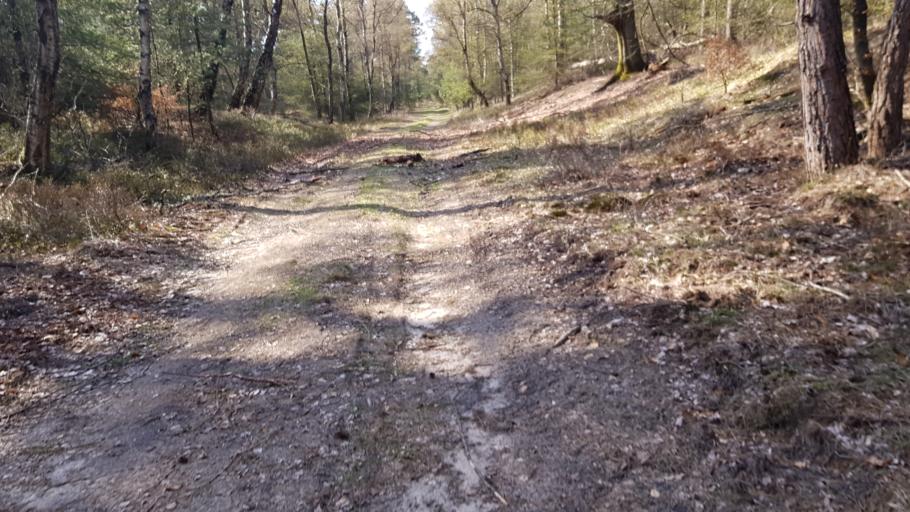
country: NL
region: Gelderland
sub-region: Gemeente Apeldoorn
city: Loenen
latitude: 52.0833
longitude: 5.9744
